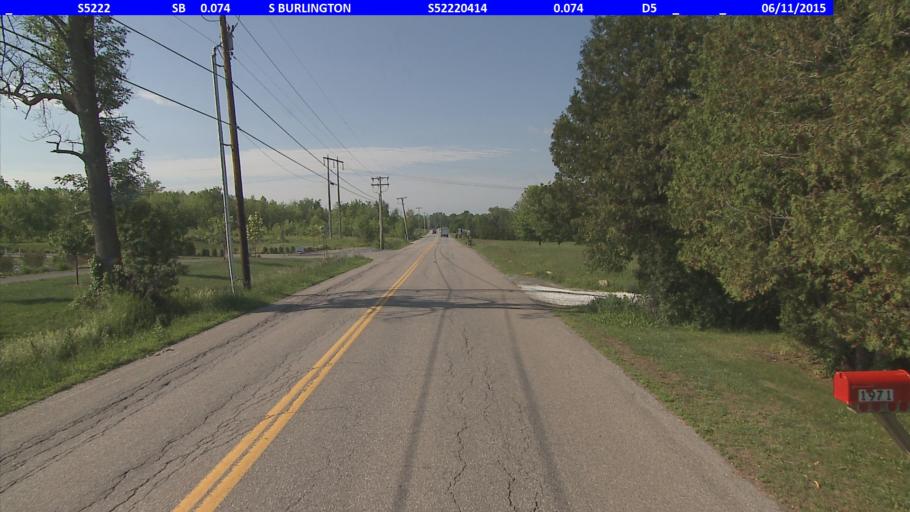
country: US
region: Vermont
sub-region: Chittenden County
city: South Burlington
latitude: 44.4177
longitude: -73.1966
